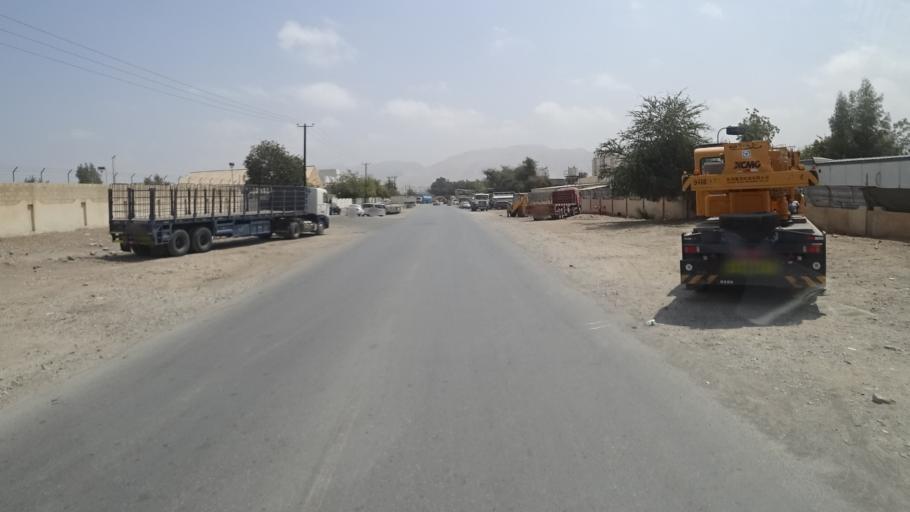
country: OM
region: Muhafazat Masqat
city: Bawshar
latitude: 23.5766
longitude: 58.3723
